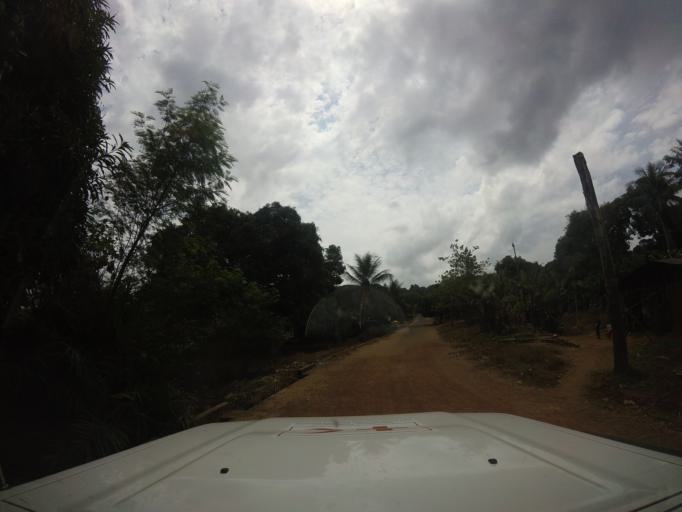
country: LR
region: Grand Cape Mount
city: Robertsport
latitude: 6.7529
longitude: -11.3780
